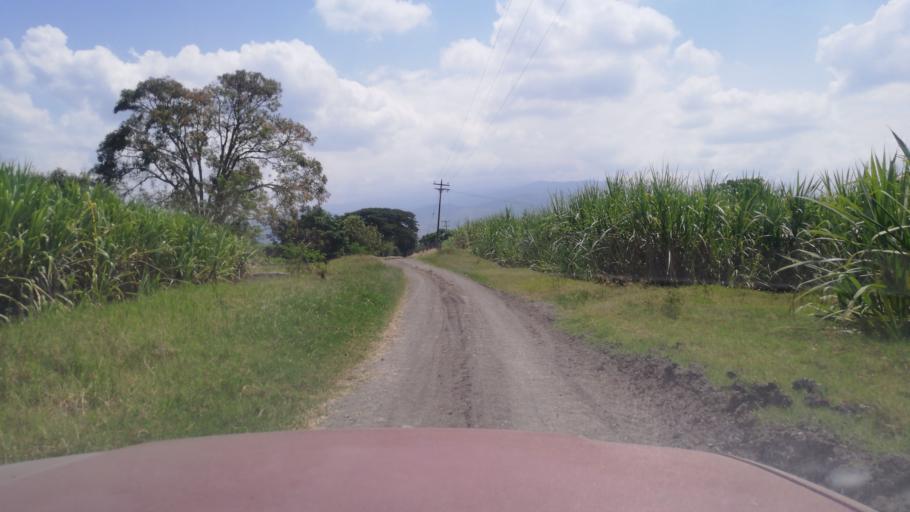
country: CO
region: Valle del Cauca
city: San Pedro
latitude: 3.9936
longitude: -76.2676
